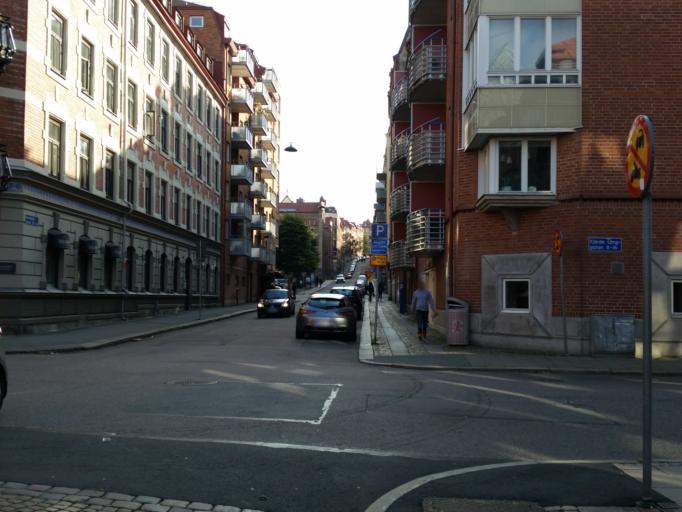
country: SE
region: Vaestra Goetaland
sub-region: Goteborg
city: Goeteborg
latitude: 57.6980
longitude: 11.9497
